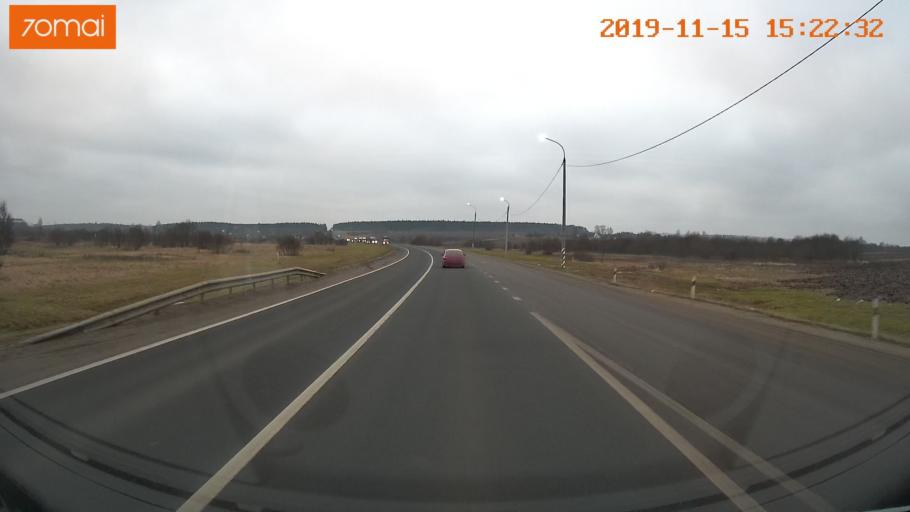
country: RU
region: Jaroslavl
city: Danilov
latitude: 58.2046
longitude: 40.1345
